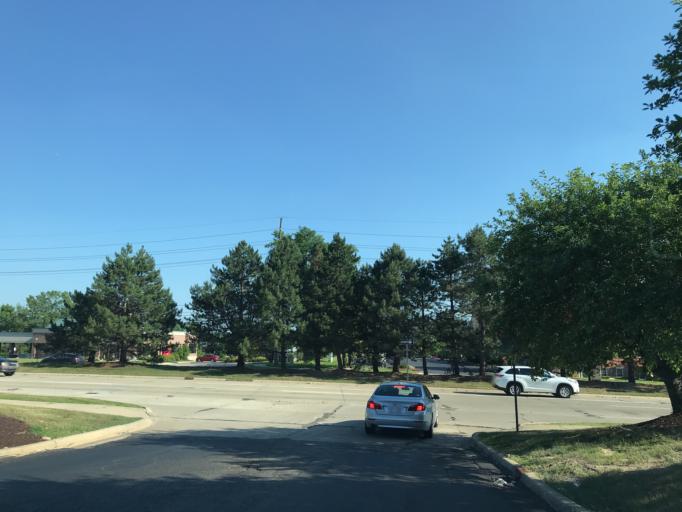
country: US
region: Michigan
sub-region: Oakland County
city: Farmington Hills
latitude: 42.4981
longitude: -83.4214
